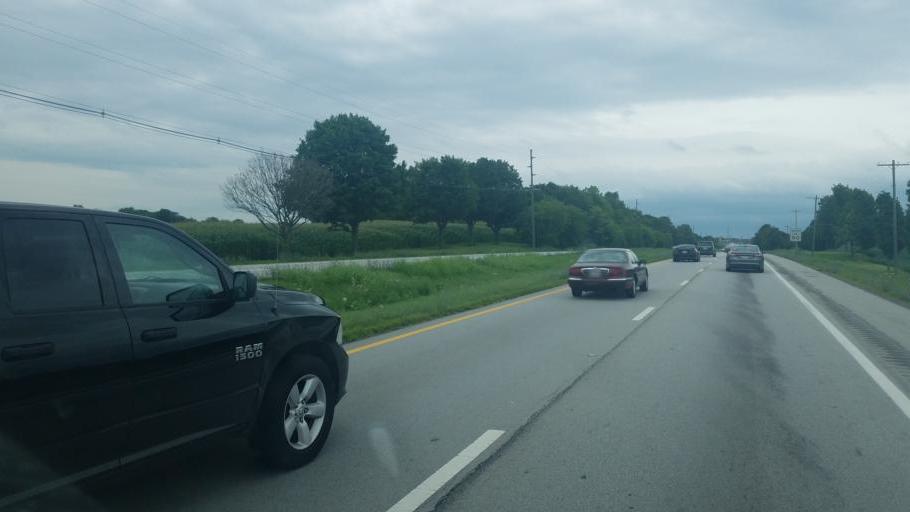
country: US
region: Ohio
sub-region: Franklin County
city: Obetz
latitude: 39.8533
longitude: -83.0030
